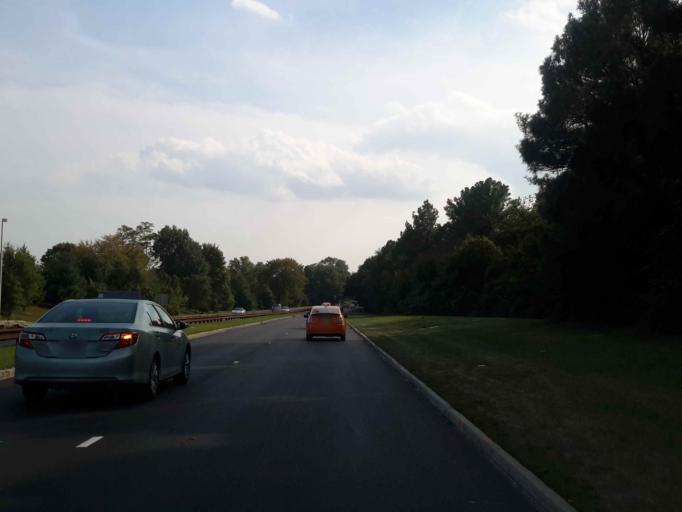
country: US
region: Washington, D.C.
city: Washington, D.C.
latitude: 38.8565
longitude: -77.0470
